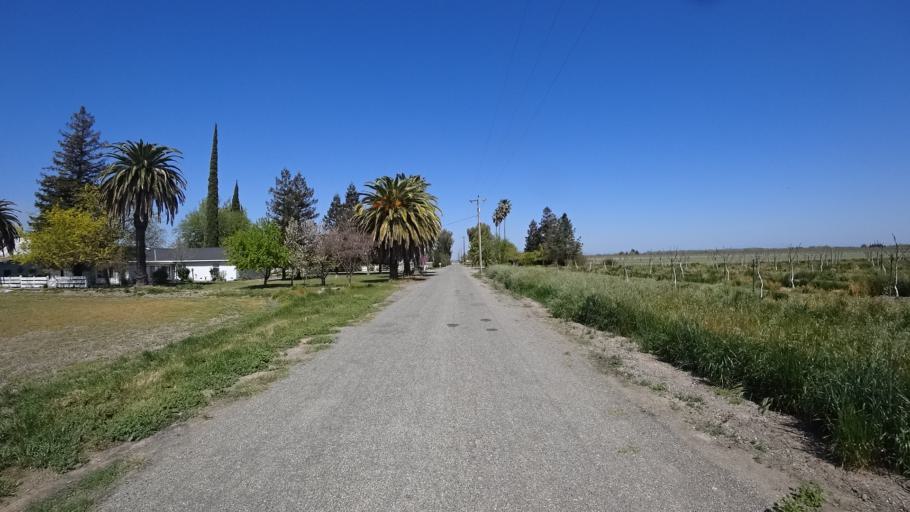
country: US
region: California
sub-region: Glenn County
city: Willows
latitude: 39.5622
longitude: -122.0184
